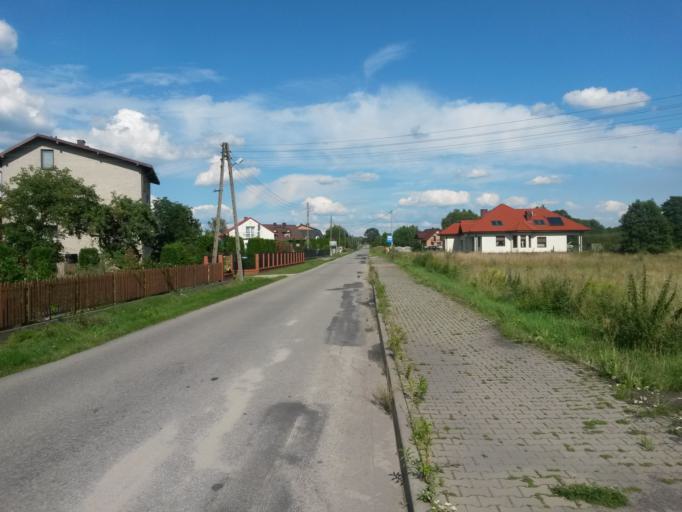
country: PL
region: Silesian Voivodeship
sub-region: Powiat bedzinski
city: Siewierz
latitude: 50.4077
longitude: 19.2121
